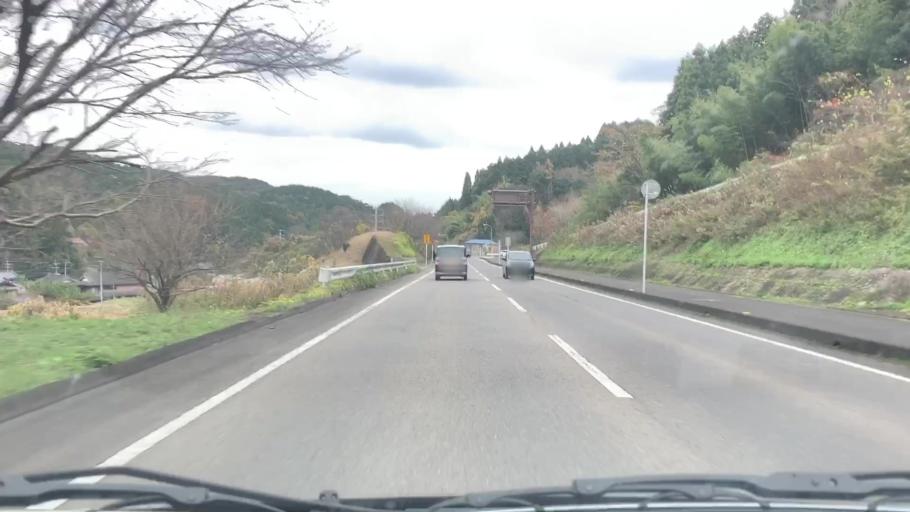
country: JP
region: Saga Prefecture
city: Ureshinomachi-shimojuku
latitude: 33.0984
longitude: 130.0399
